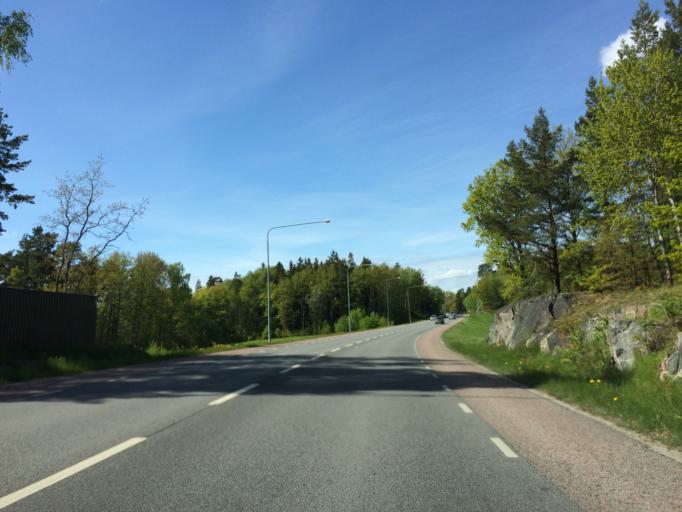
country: SE
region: Stockholm
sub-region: Norrtalje Kommun
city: Bergshamra
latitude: 59.4203
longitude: 18.0051
